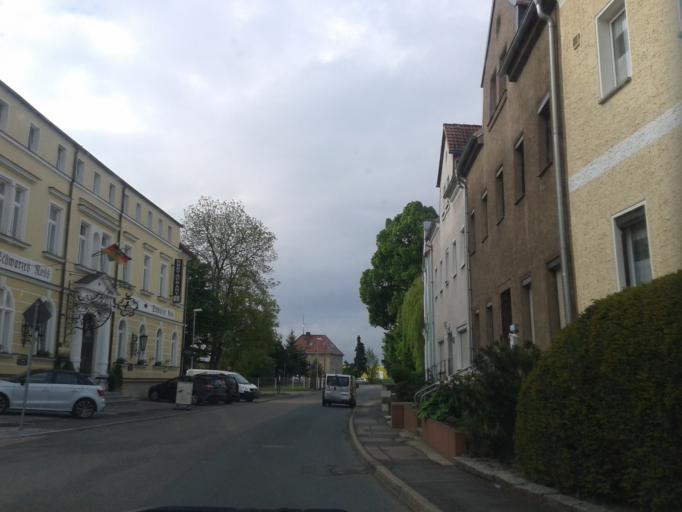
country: DE
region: Saxony
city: Nossen
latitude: 51.0294
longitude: 13.3068
